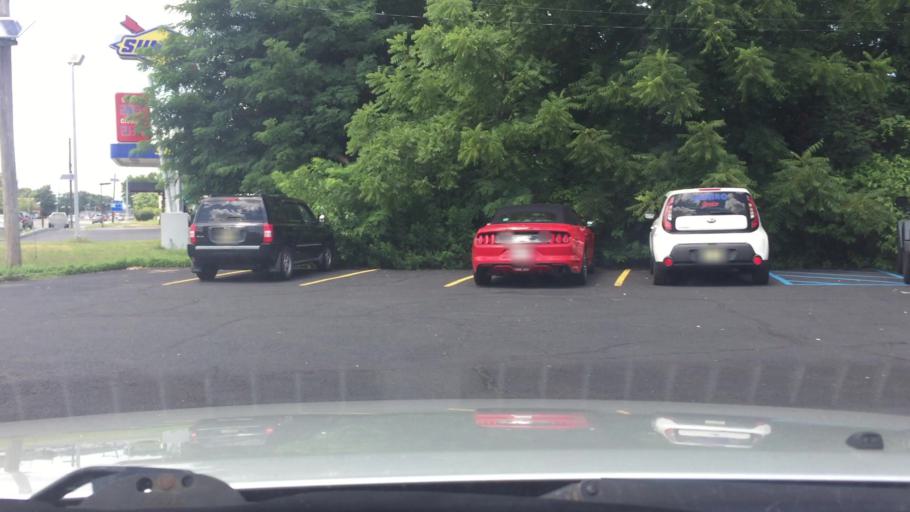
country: US
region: New Jersey
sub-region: Middlesex County
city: Old Bridge
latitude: 40.4216
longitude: -74.3767
